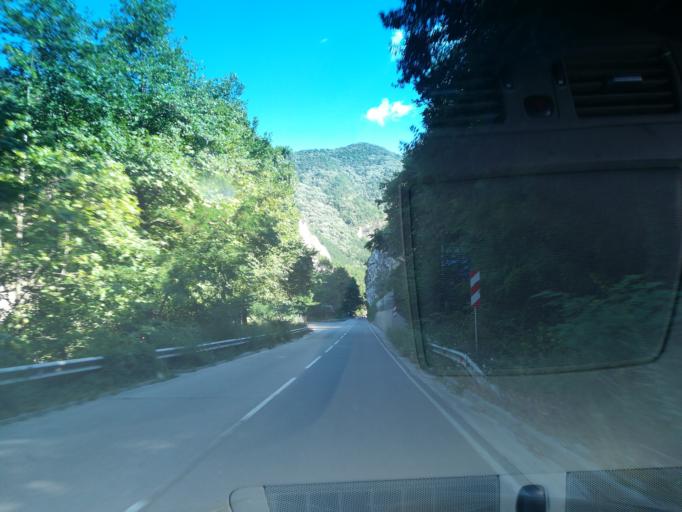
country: BG
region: Plovdiv
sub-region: Obshtina Asenovgrad
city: Asenovgrad
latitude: 41.9884
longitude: 24.8742
